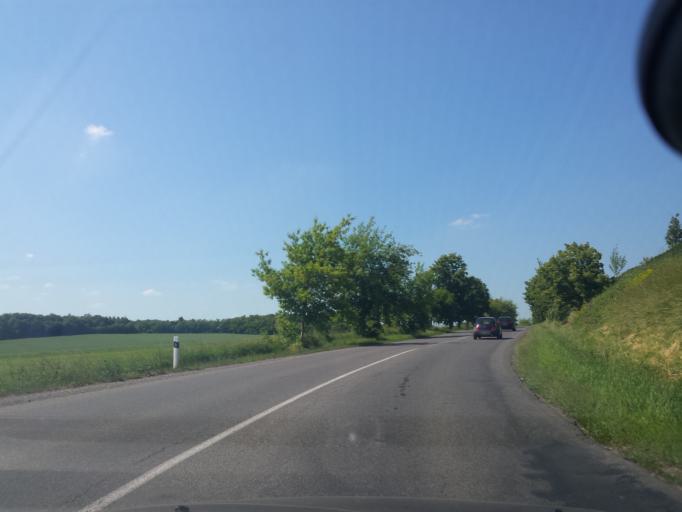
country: CZ
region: Central Bohemia
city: Velke Prilepy
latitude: 50.1529
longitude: 14.3178
